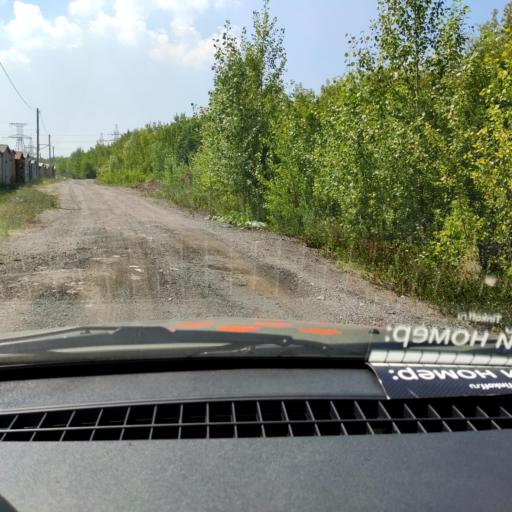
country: RU
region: Bashkortostan
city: Ufa
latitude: 54.7938
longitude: 56.0974
